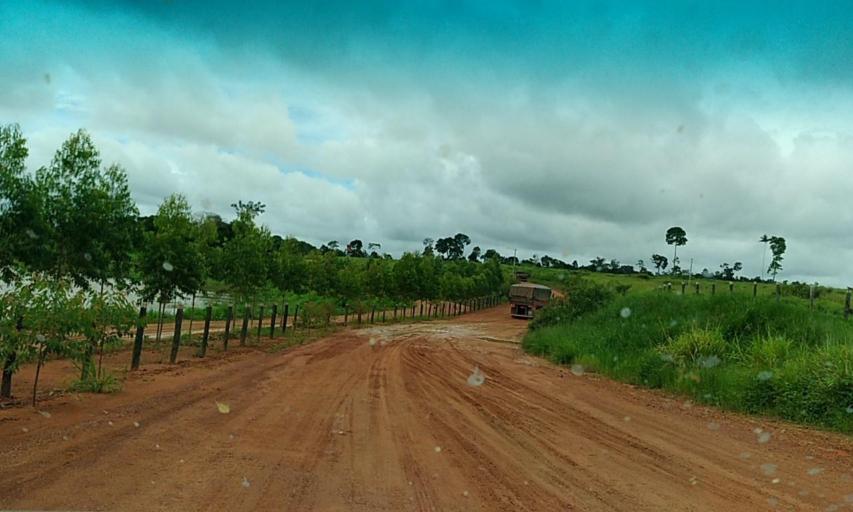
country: BR
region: Para
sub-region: Altamira
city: Altamira
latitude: -3.0535
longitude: -51.7248
